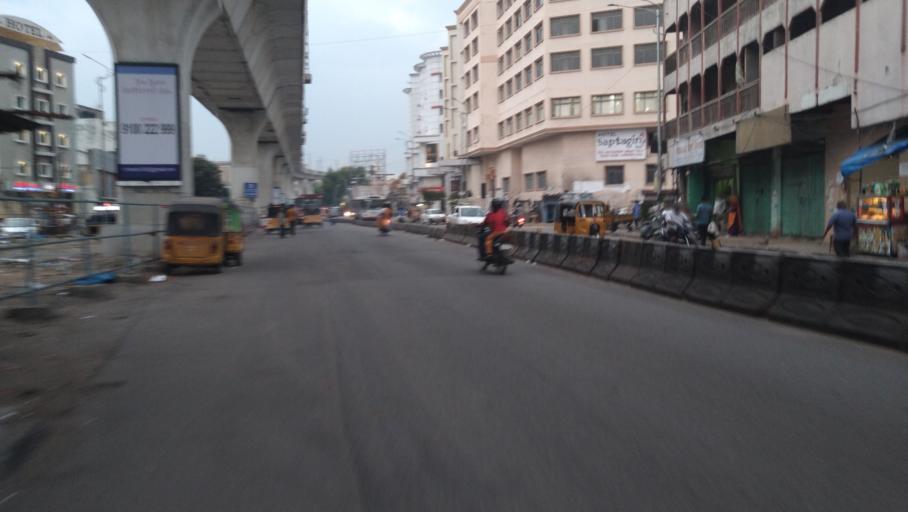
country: IN
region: Telangana
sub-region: Hyderabad
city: Malkajgiri
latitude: 17.4374
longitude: 78.4998
